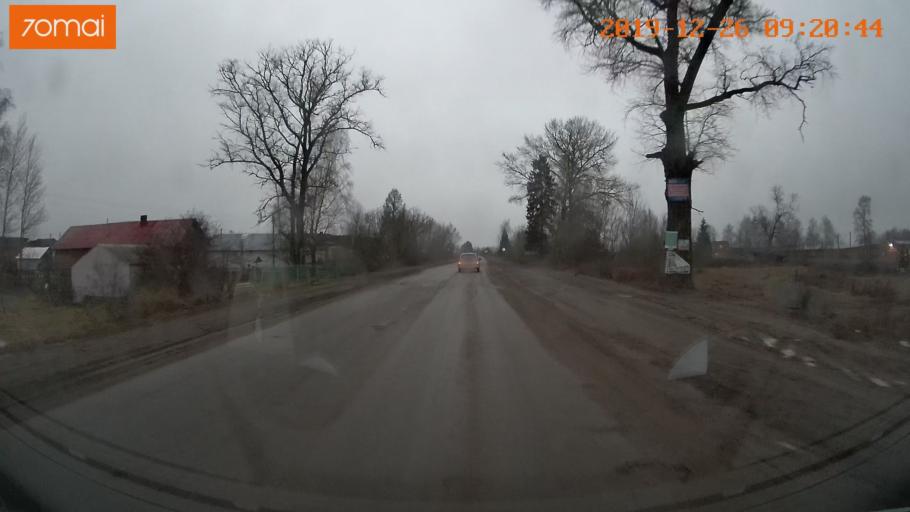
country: RU
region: Vologda
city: Gryazovets
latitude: 58.9638
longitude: 40.2279
